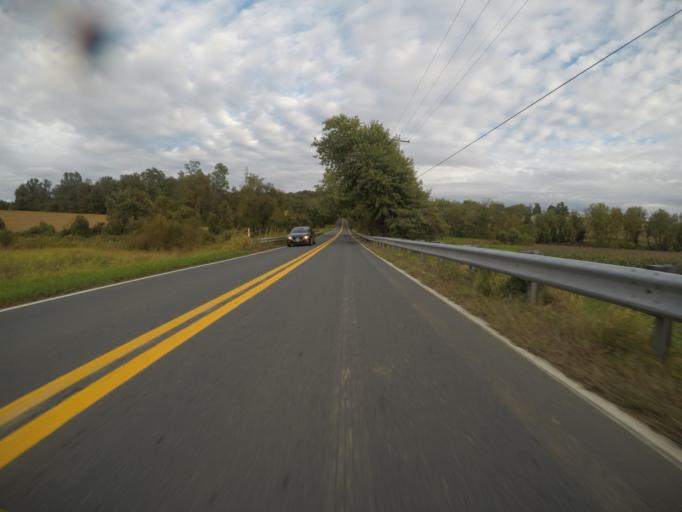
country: US
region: Maryland
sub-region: Carroll County
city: Hampstead
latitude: 39.5689
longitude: -76.8670
